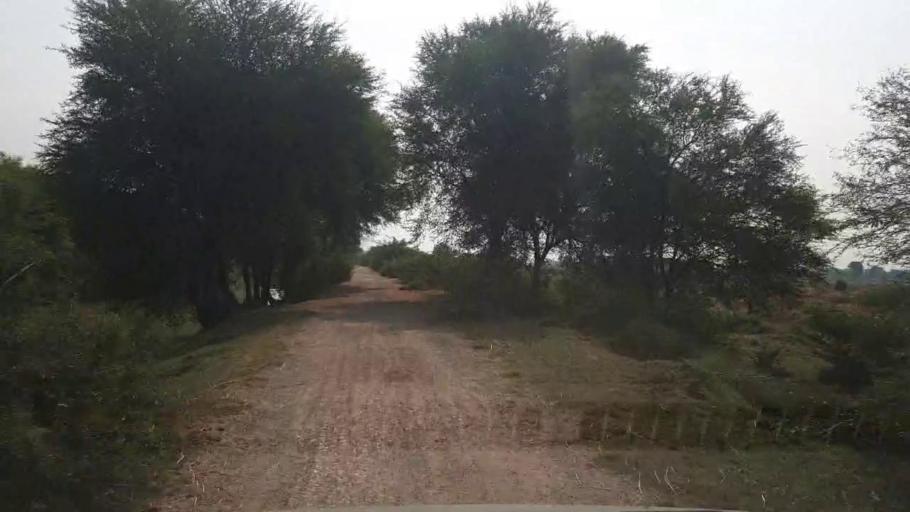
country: PK
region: Sindh
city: Tando Muhammad Khan
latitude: 25.1208
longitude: 68.4385
